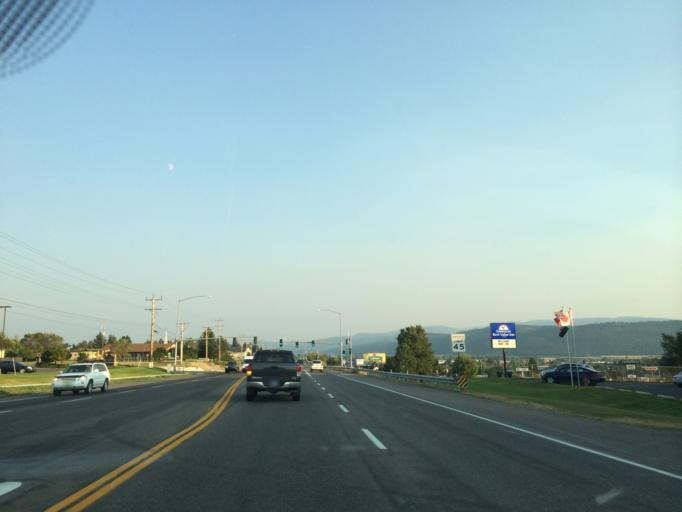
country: US
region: Montana
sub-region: Flathead County
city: Kalispell
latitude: 48.2163
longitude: -114.3293
